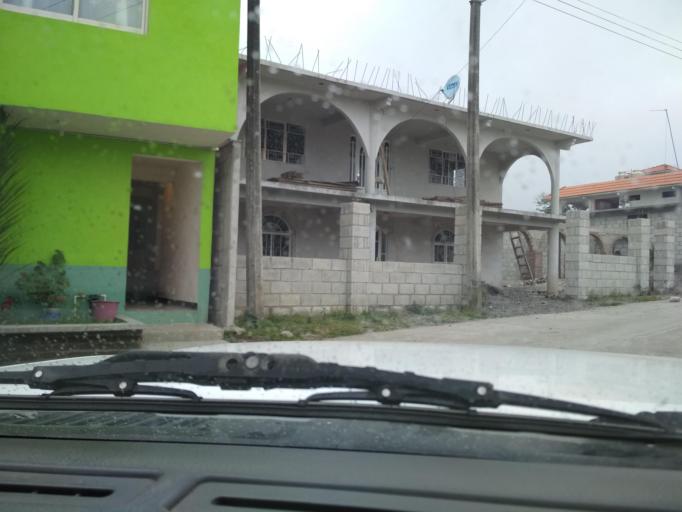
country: MX
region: Veracruz
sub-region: La Perla
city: Chilapa
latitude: 18.9880
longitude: -97.1484
